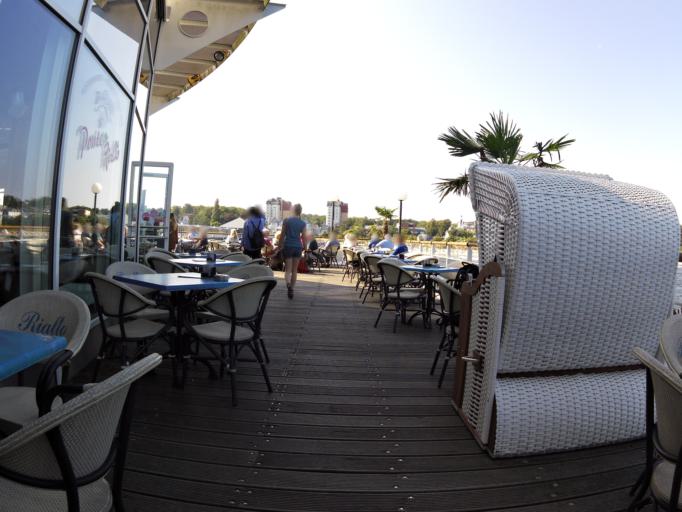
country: DE
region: Mecklenburg-Vorpommern
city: Seebad Heringsdorf
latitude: 53.9584
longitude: 14.1745
